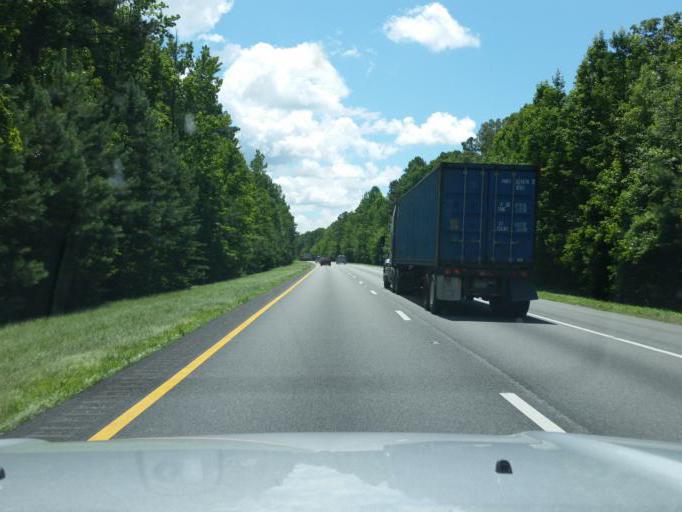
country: US
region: Virginia
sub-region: King William County
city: West Point
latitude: 37.4300
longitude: -76.8418
